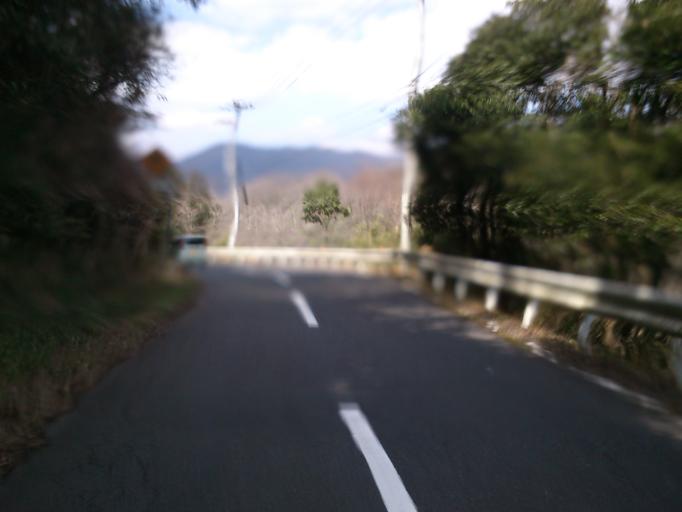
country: JP
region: Mie
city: Ueno-ebisumachi
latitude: 34.7580
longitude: 136.0106
